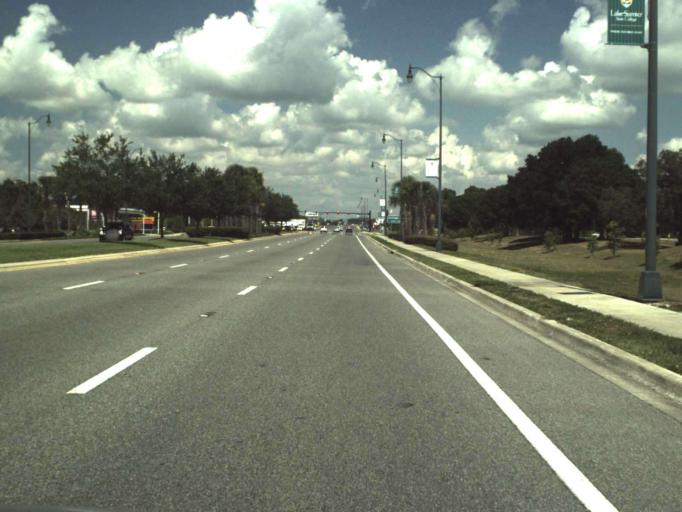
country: US
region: Florida
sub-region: Lake County
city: Silver Lake
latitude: 28.8261
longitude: -81.7966
